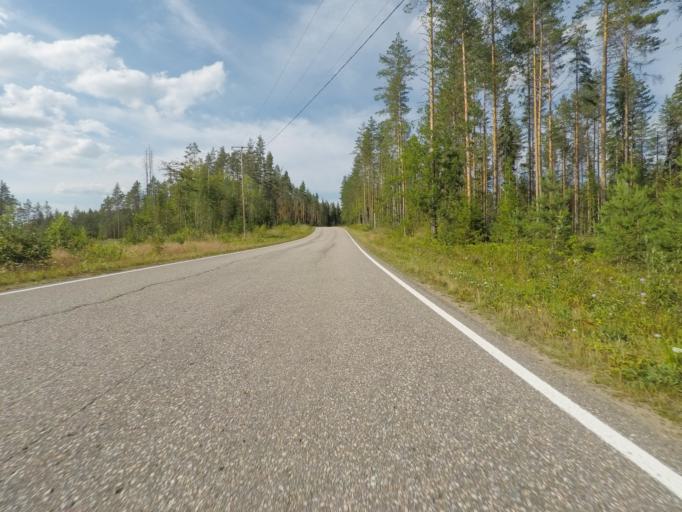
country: FI
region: Southern Savonia
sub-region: Savonlinna
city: Sulkava
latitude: 61.7657
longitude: 28.2365
